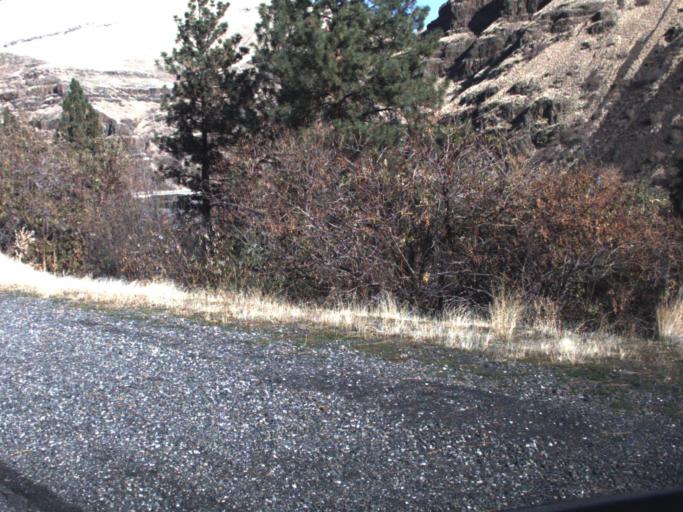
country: US
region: Washington
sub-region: Asotin County
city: Asotin
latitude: 46.0359
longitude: -117.2553
